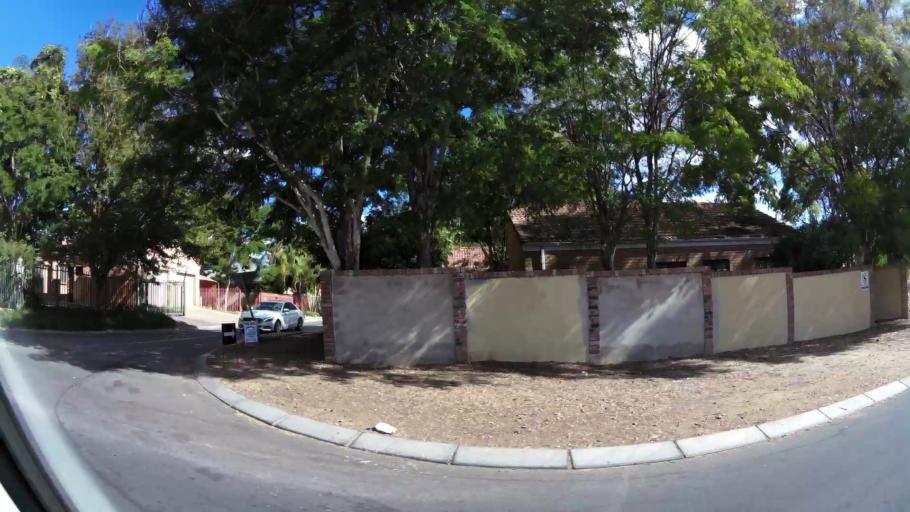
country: ZA
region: Limpopo
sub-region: Capricorn District Municipality
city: Polokwane
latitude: -23.8816
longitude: 29.4707
